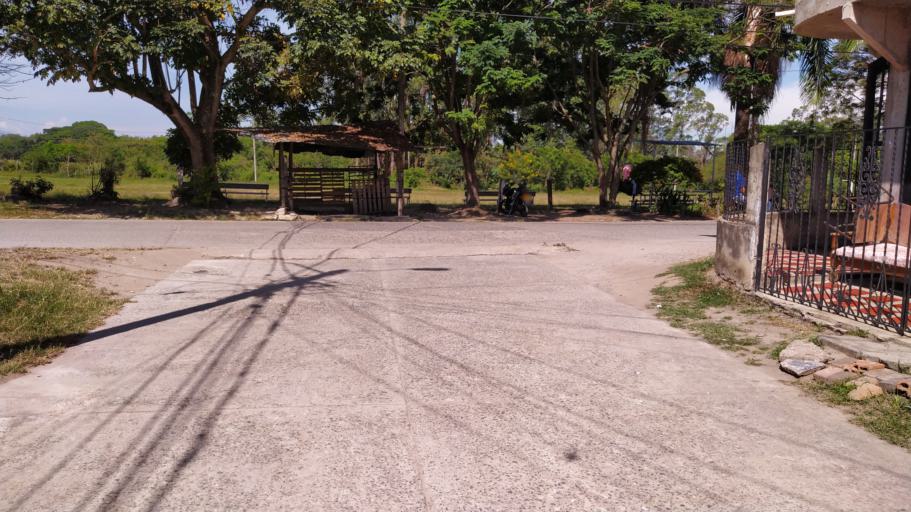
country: CO
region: Valle del Cauca
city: Florida
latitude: 3.3189
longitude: -76.2233
